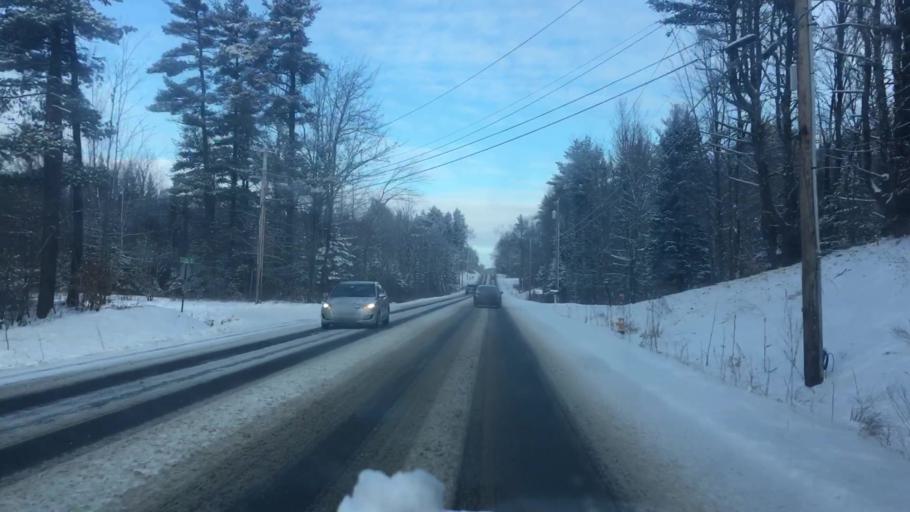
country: US
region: Maine
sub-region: Cumberland County
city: North Windham
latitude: 43.8027
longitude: -70.4404
